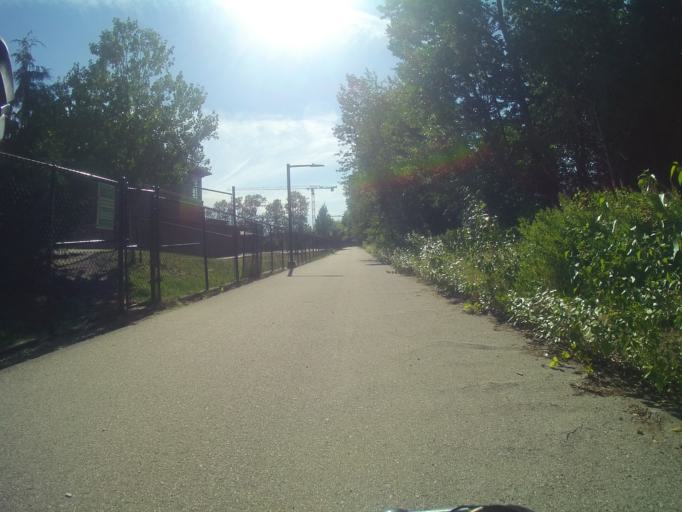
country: CA
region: British Columbia
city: Vancouver
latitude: 49.2177
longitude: -123.1084
